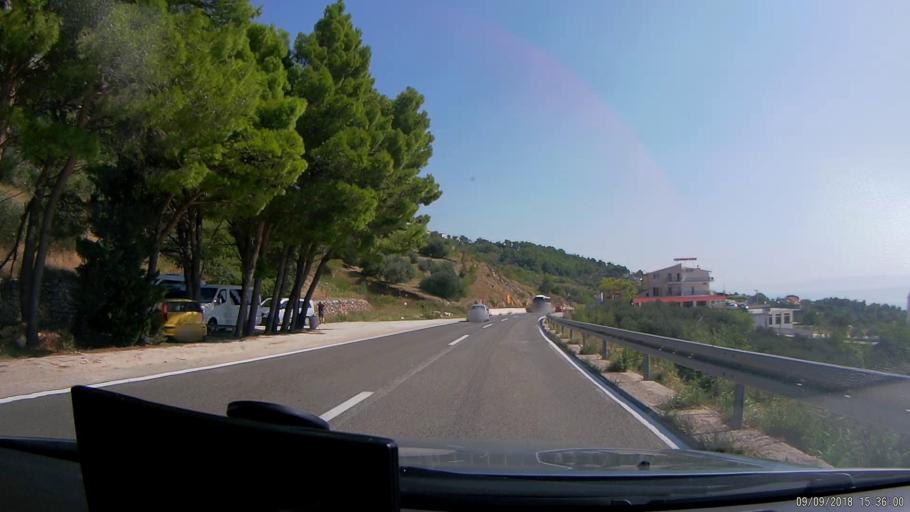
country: HR
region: Splitsko-Dalmatinska
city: Donja Brela
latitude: 43.3817
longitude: 16.9203
